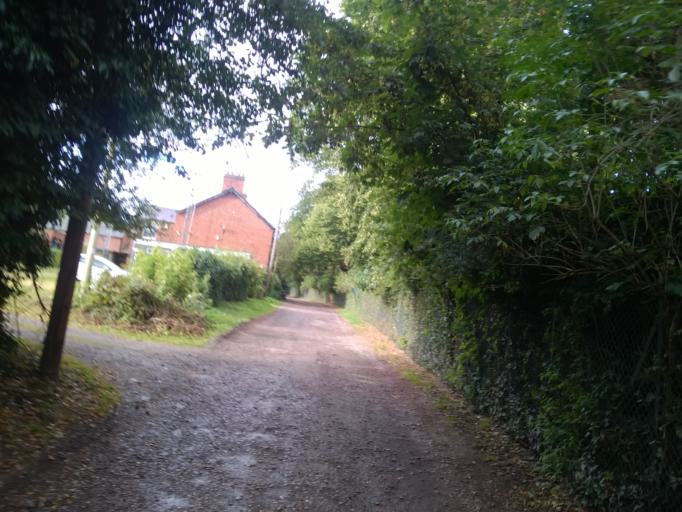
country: GB
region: England
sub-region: Leicestershire
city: Glenfield
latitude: 52.6520
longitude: -1.1701
